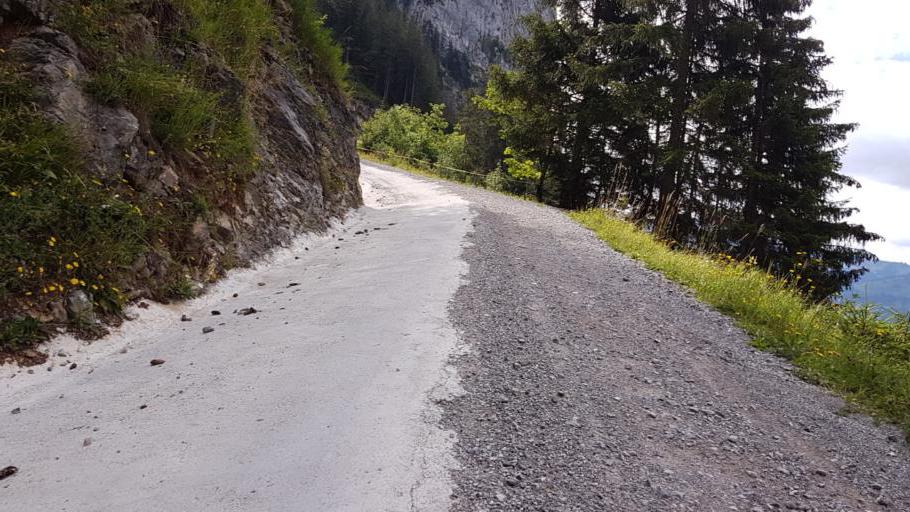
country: CH
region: Bern
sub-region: Obersimmental-Saanen District
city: Boltigen
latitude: 46.6878
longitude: 7.4476
